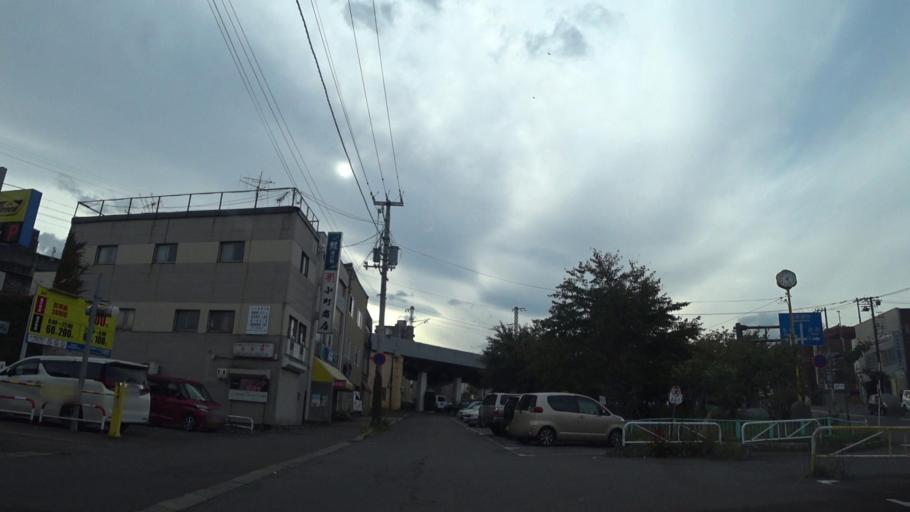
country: JP
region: Hokkaido
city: Otaru
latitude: 43.1938
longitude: 140.9979
